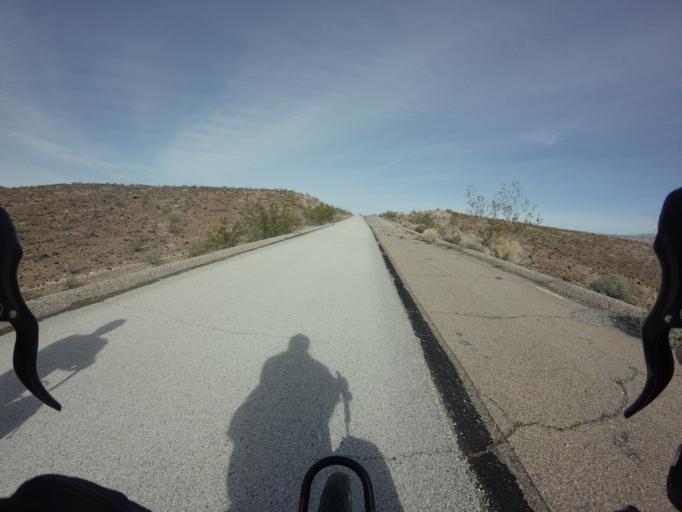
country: US
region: Nevada
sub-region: Clark County
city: Boulder City
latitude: 36.0949
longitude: -114.8431
